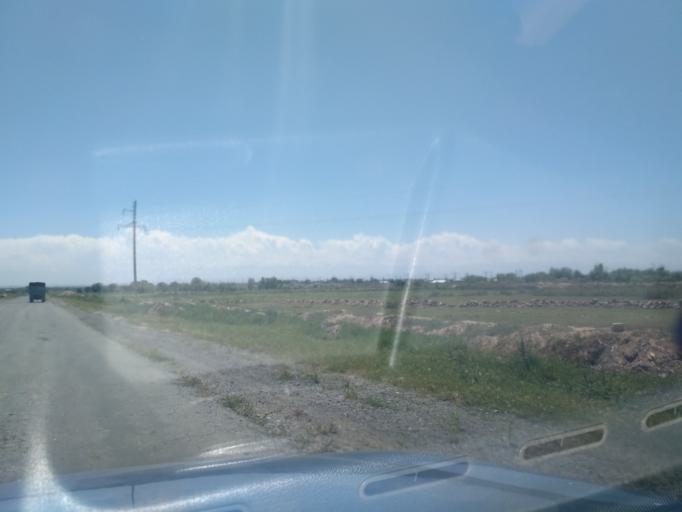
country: TJ
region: Viloyati Sughd
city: Zafarobod
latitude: 40.2277
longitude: 68.8497
